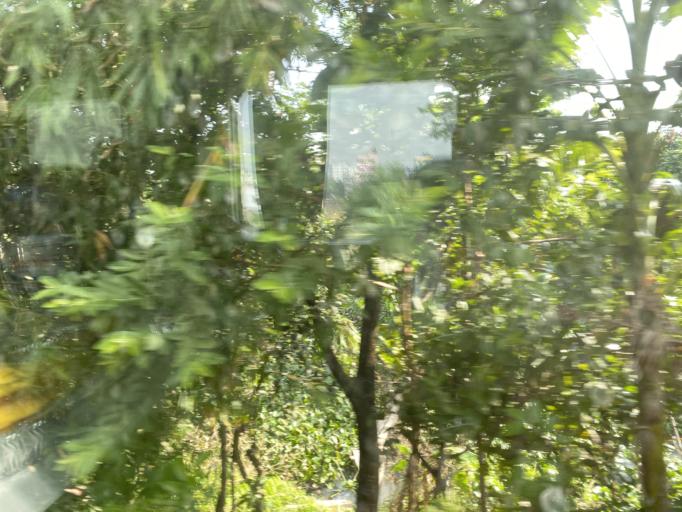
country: BD
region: Chittagong
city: Nabinagar
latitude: 23.9614
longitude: 91.1185
